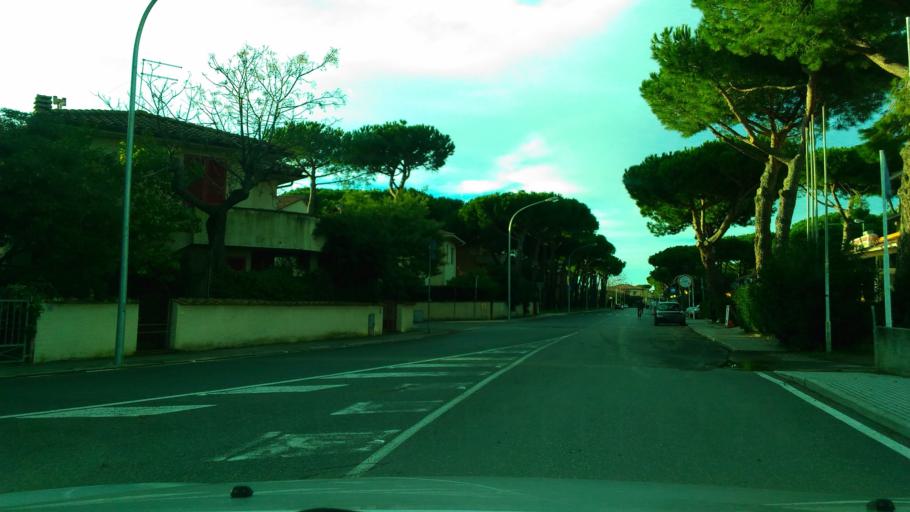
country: IT
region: Tuscany
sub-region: Provincia di Livorno
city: Cecina
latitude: 43.2957
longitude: 10.5029
